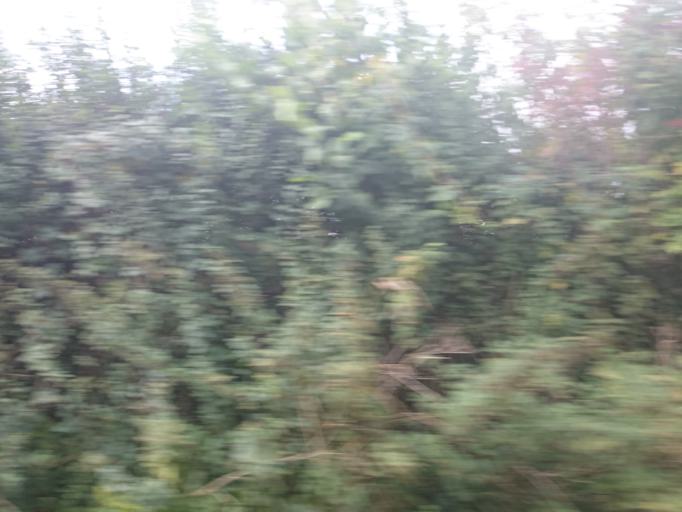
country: GB
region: England
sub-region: Gloucestershire
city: Coates
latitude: 51.7566
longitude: -2.0268
